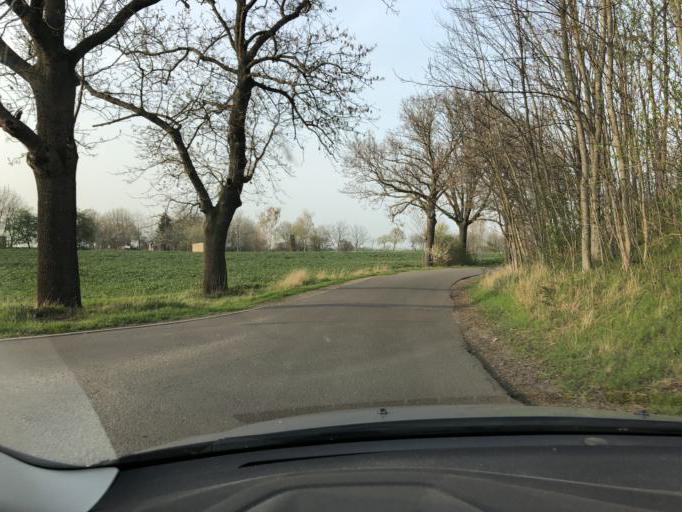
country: DE
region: Saxony-Anhalt
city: Brehna
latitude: 51.5616
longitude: 12.2172
